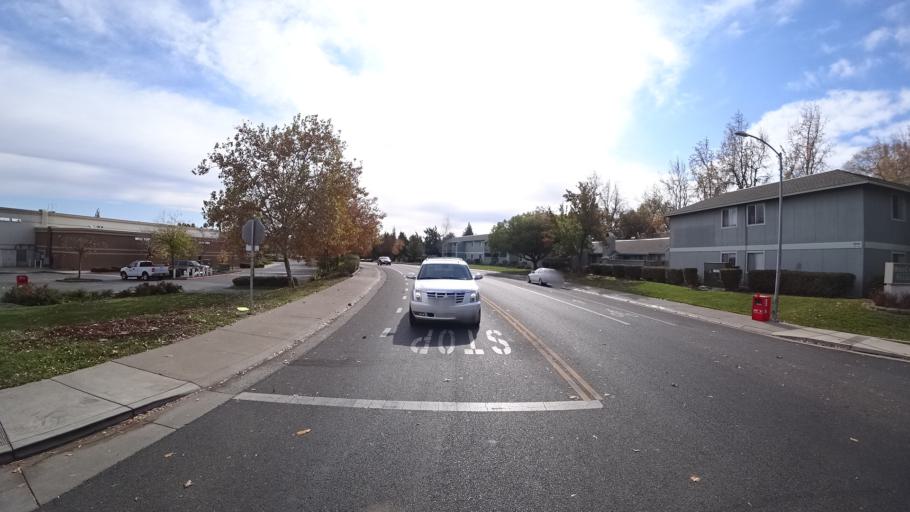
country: US
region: California
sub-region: Sacramento County
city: Fair Oaks
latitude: 38.6733
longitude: -121.2762
